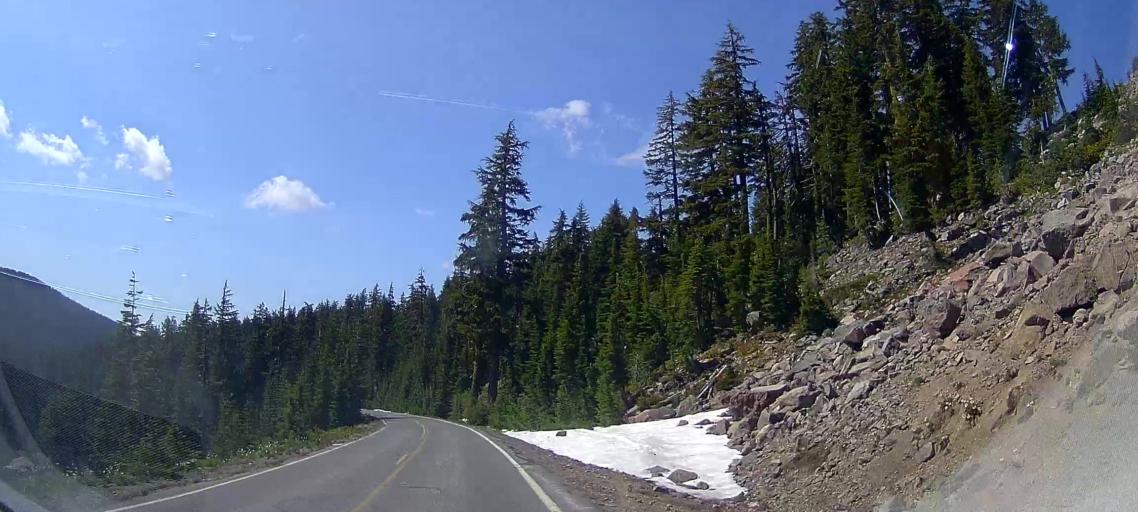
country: US
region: Oregon
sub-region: Klamath County
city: Klamath Falls
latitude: 42.8961
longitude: -122.0999
